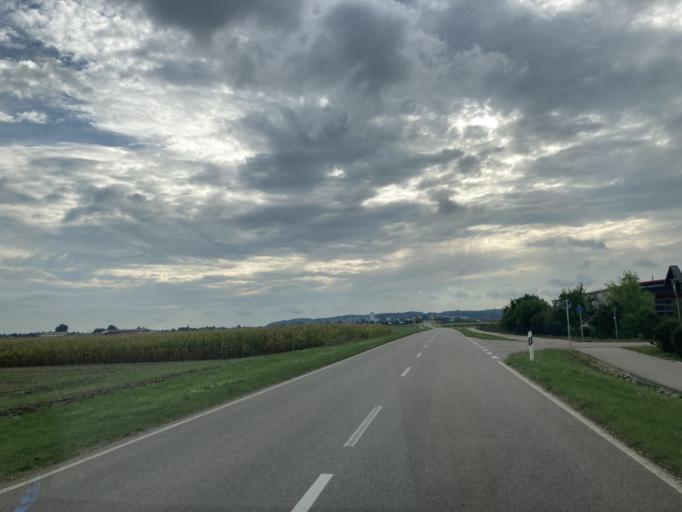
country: DE
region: Bavaria
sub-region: Swabia
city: Medlingen
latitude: 48.5662
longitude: 10.3159
